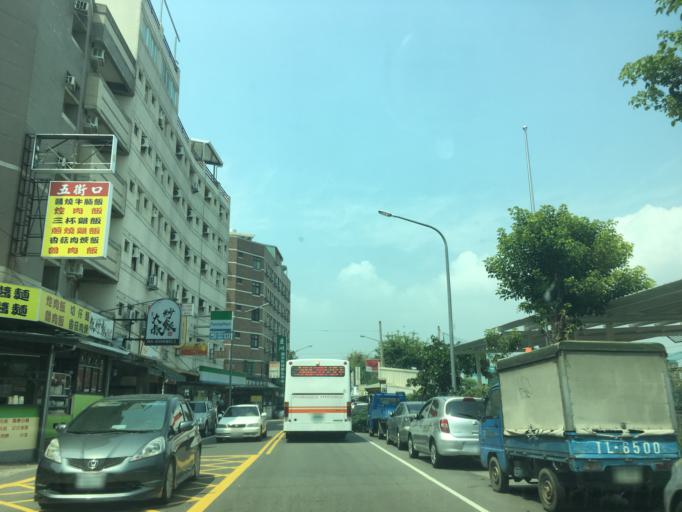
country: TW
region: Taiwan
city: Zhongxing New Village
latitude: 24.0443
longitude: 120.6885
